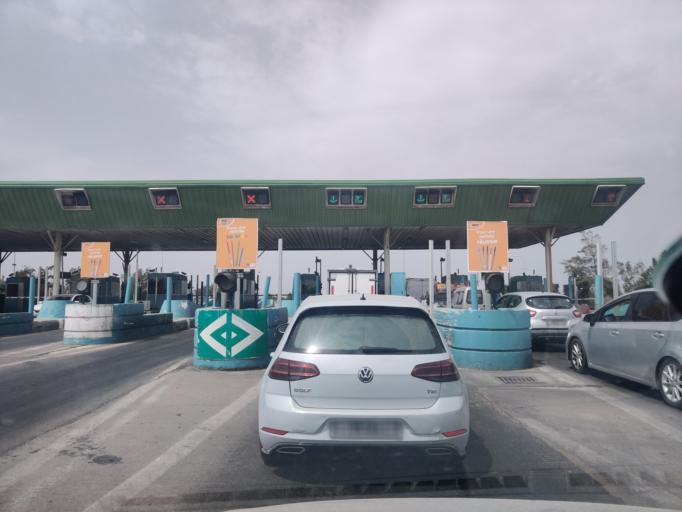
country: TN
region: Susah
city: Sidi Bou Ali
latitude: 36.0034
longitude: 10.4358
